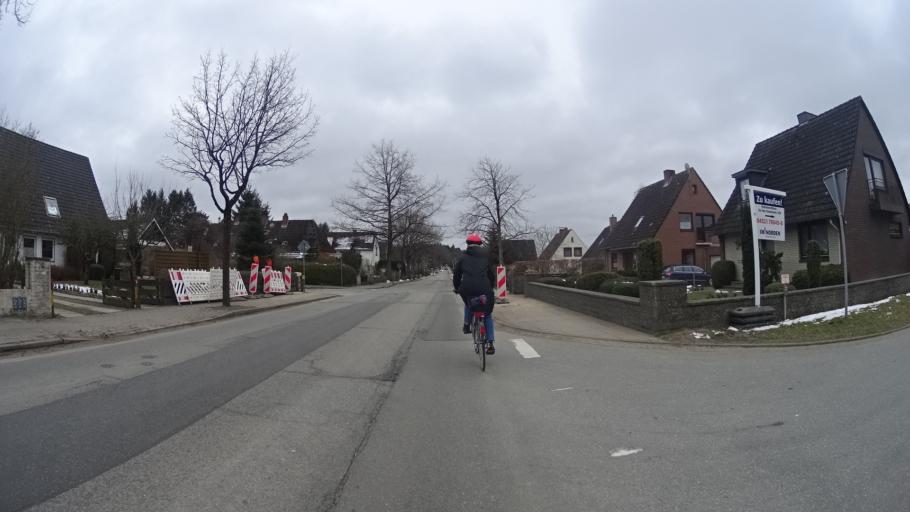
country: DE
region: Schleswig-Holstein
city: Malente
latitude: 54.1839
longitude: 10.5634
